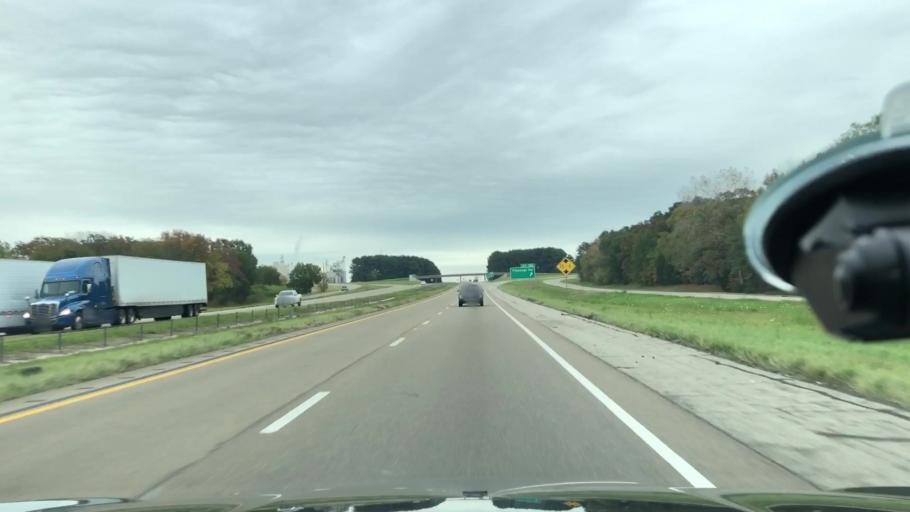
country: US
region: Texas
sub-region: Titus County
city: Mount Pleasant
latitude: 33.1594
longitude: -95.0805
